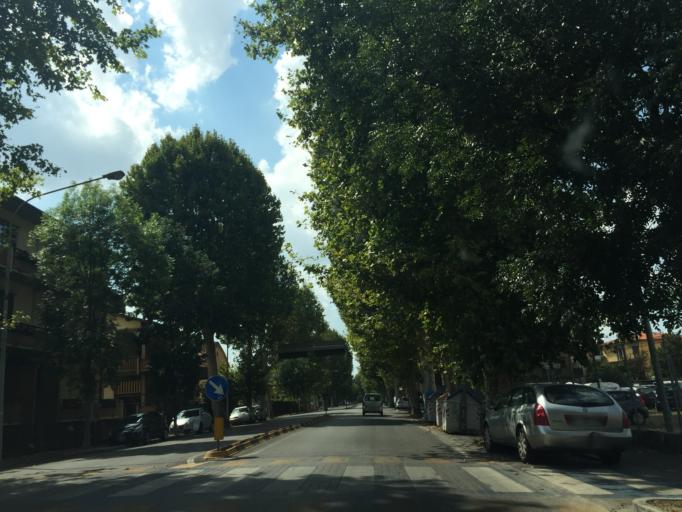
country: IT
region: Tuscany
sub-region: Province of Florence
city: Mantignano-Ugnano
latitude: 43.7951
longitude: 11.1978
